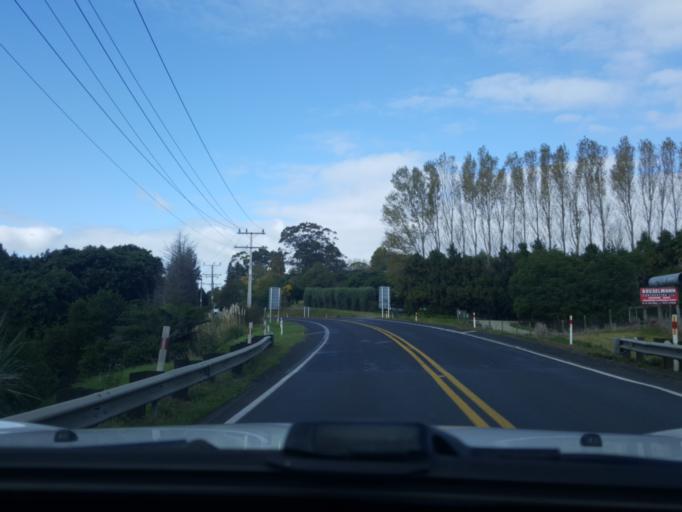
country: NZ
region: Bay of Plenty
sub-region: Western Bay of Plenty District
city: Katikati
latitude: -37.6462
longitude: 175.9890
